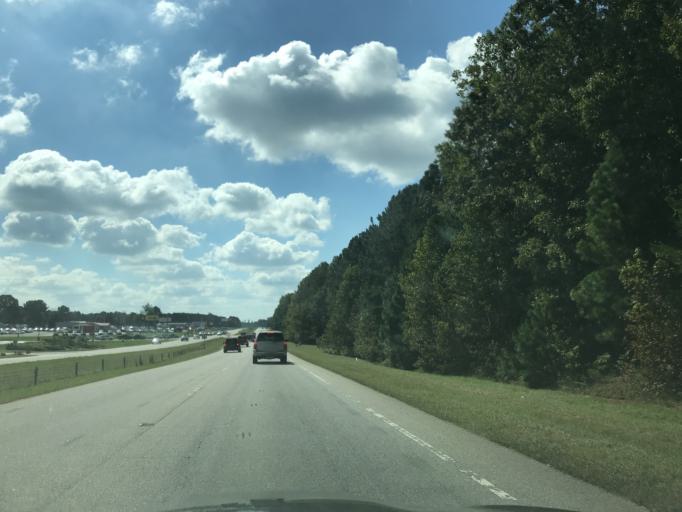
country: US
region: North Carolina
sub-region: Franklin County
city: Youngsville
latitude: 36.0274
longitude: -78.5079
